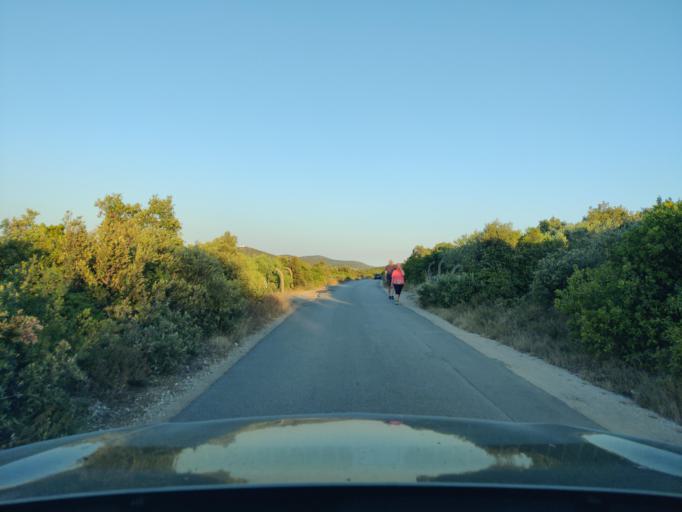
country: HR
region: Sibensko-Kniniska
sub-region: Grad Sibenik
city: Tisno
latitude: 43.8082
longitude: 15.6408
